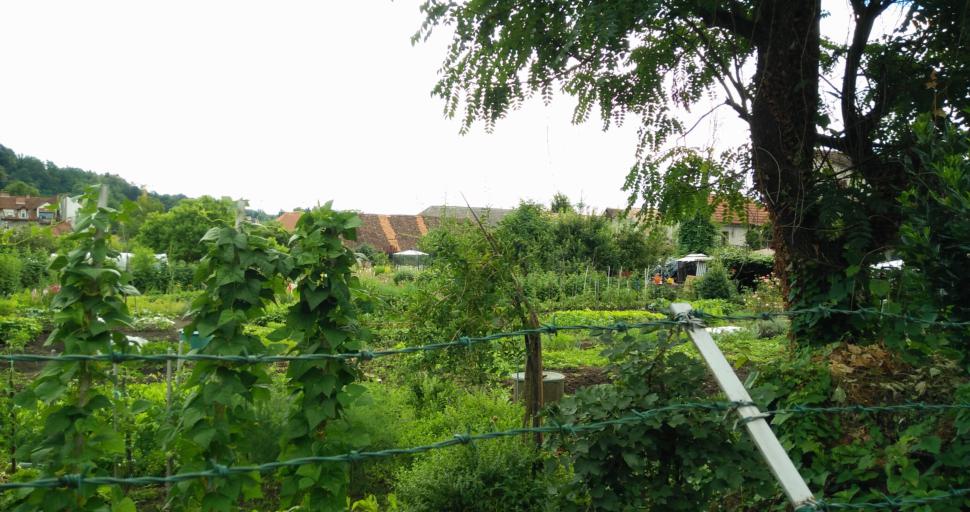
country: SI
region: Ljubljana
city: Ljubljana
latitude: 46.0457
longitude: 14.5026
